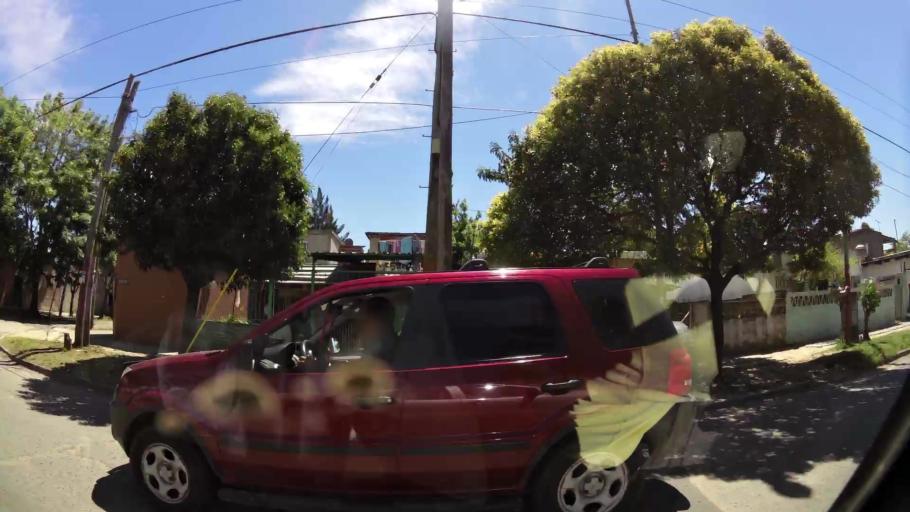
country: AR
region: Buenos Aires
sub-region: Partido de Quilmes
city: Quilmes
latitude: -34.7314
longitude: -58.3227
